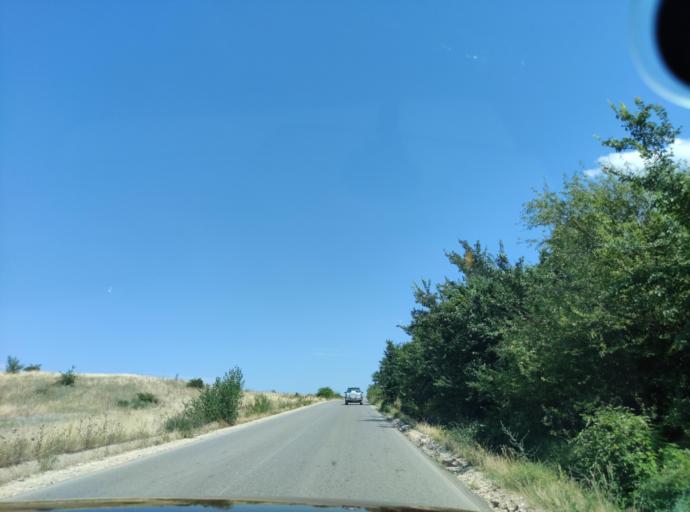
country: BG
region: Pleven
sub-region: Obshtina Cherven Bryag
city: Koynare
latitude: 43.3732
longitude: 24.0604
